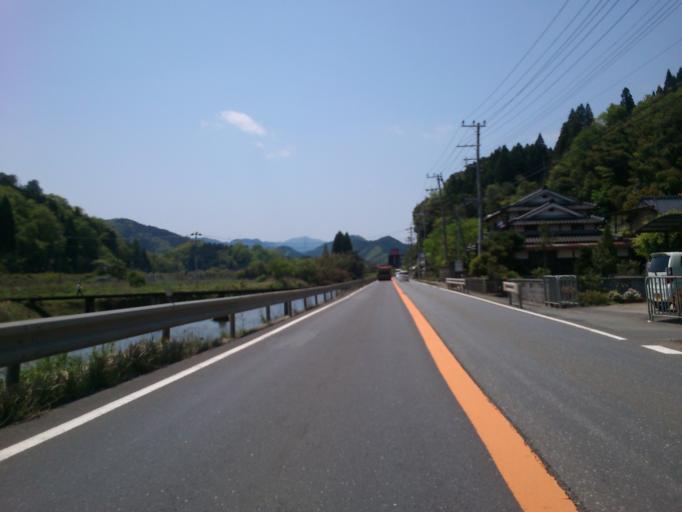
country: JP
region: Kyoto
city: Fukuchiyama
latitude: 35.3281
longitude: 135.0644
